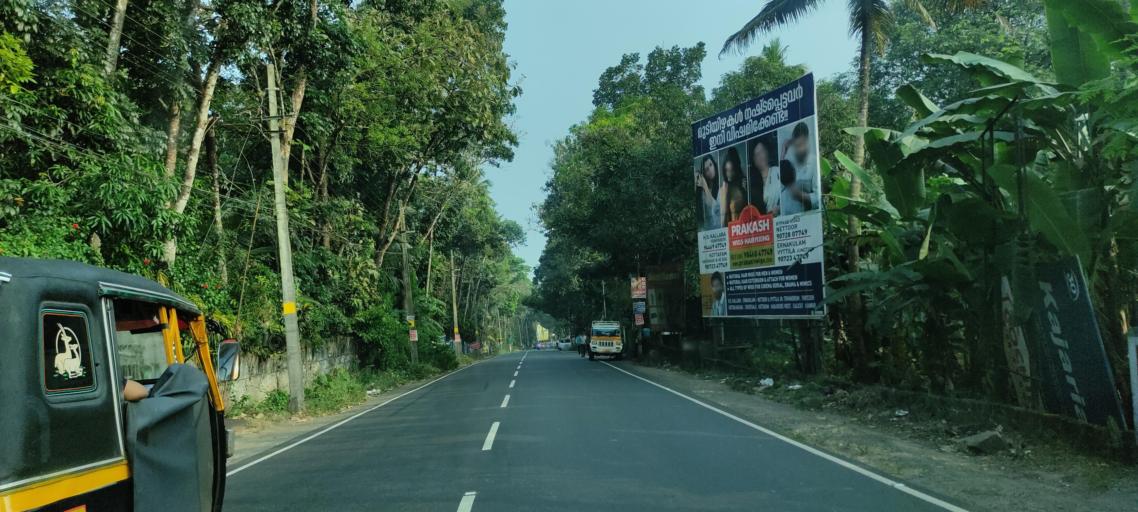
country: IN
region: Kerala
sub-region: Kottayam
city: Vaikam
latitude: 9.7592
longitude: 76.4942
